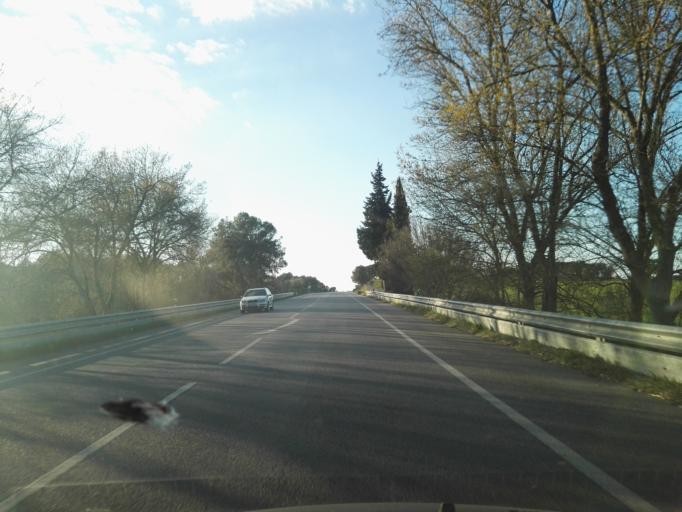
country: PT
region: Evora
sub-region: Montemor-O-Novo
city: Montemor-o-Novo
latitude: 38.6207
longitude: -8.0902
